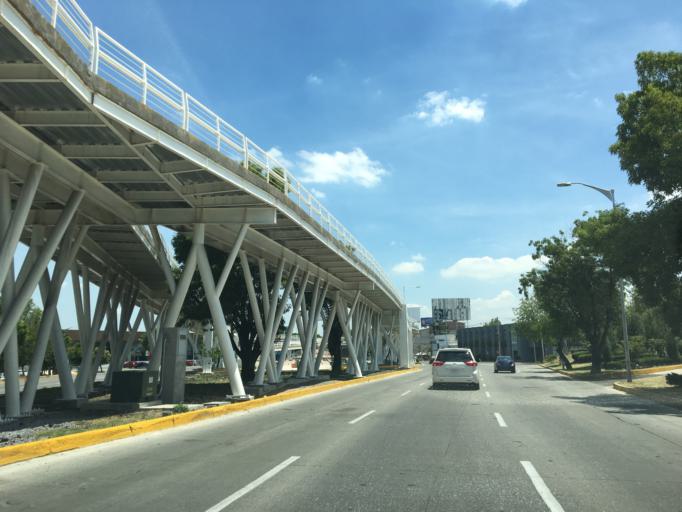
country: MX
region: Puebla
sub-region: Cuautlancingo
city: Sanctorum
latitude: 19.0731
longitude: -98.2272
